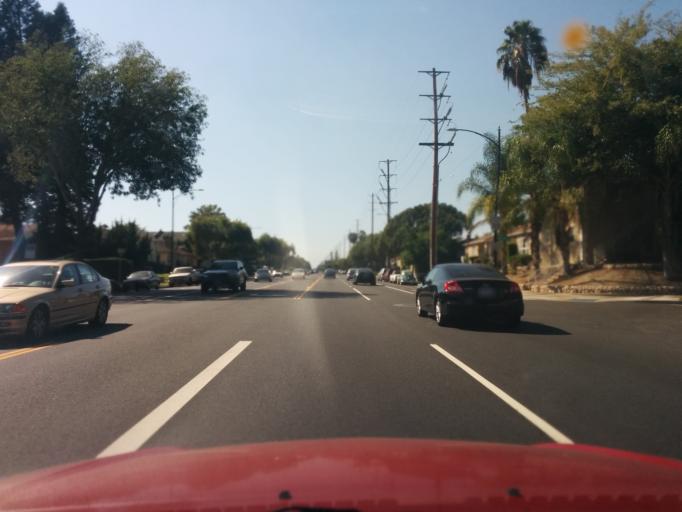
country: US
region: California
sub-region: Los Angeles County
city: Burbank
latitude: 34.1844
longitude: -118.3250
